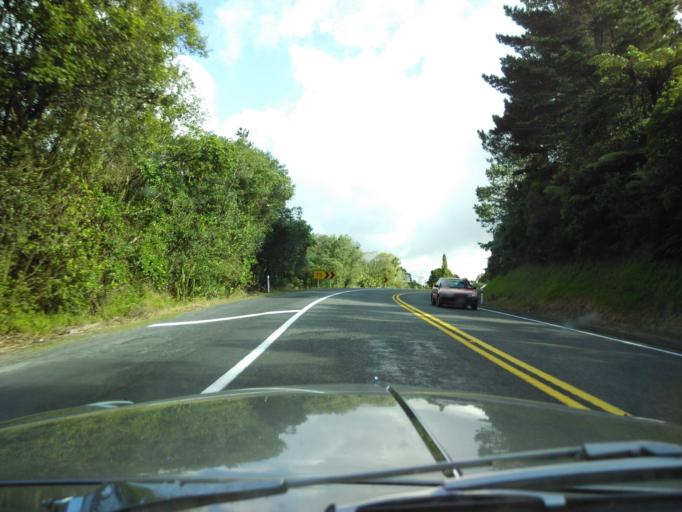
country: NZ
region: Bay of Plenty
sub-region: Western Bay of Plenty District
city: Waihi Beach
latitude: -37.4532
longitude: 175.8867
